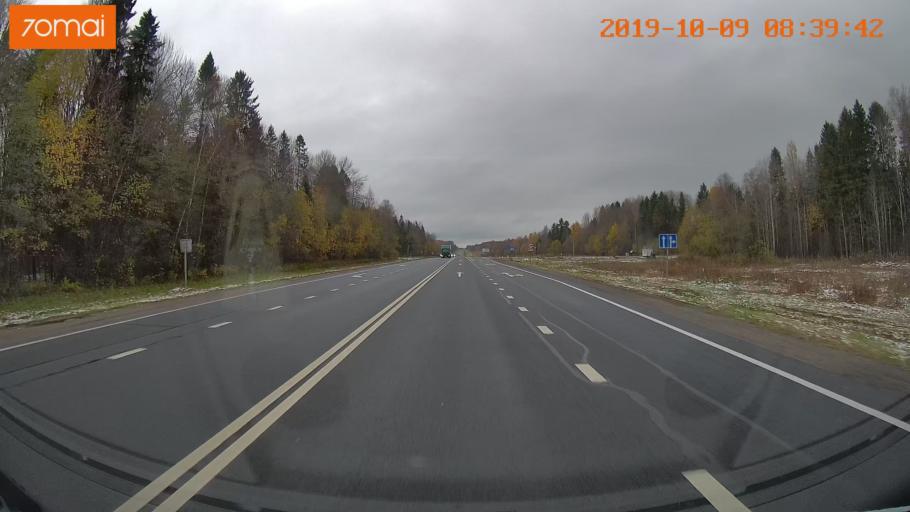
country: RU
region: Vologda
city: Gryazovets
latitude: 58.9756
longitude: 40.1497
